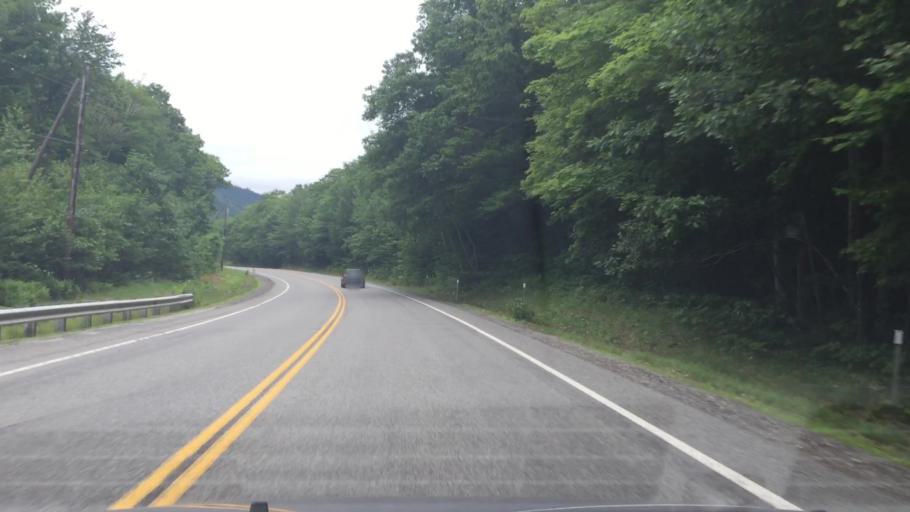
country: US
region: New Hampshire
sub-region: Carroll County
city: North Conway
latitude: 44.1268
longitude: -71.3594
